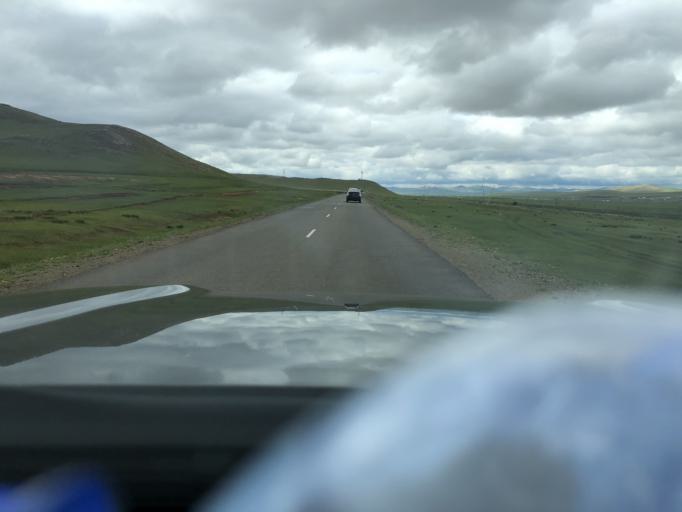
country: MN
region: Central Aimak
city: Ihsueuej
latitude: 48.0267
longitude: 106.5499
